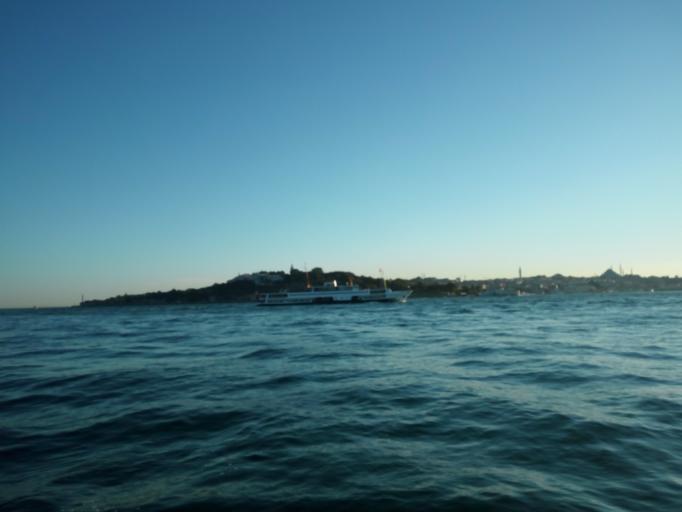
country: TR
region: Istanbul
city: Eminoenue
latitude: 41.0208
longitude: 28.9951
